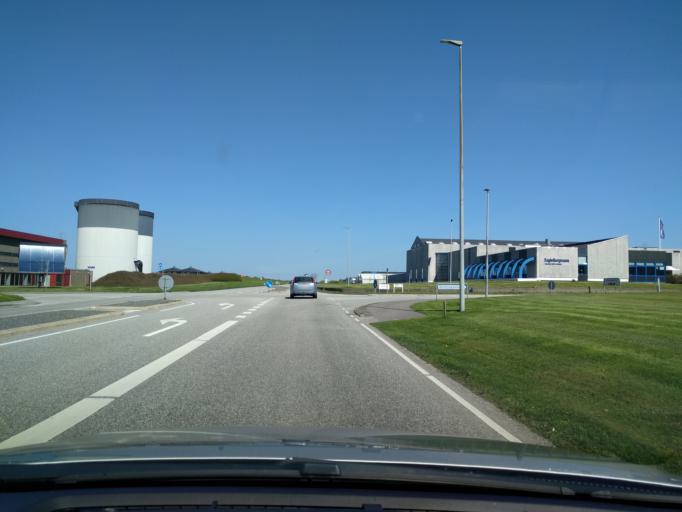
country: DK
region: Central Jutland
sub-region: Ringkobing-Skjern Kommune
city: Ringkobing
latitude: 56.0895
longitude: 8.2784
